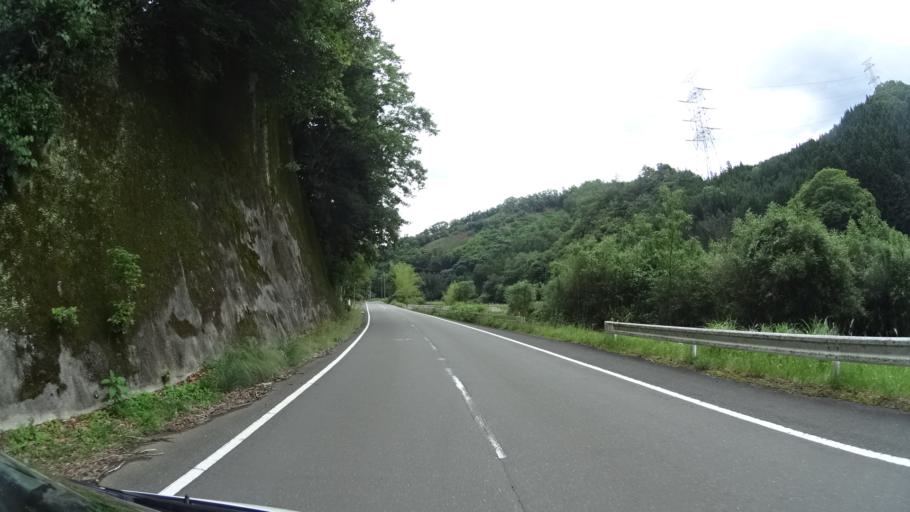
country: JP
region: Kyoto
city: Kameoka
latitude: 35.0715
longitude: 135.4093
